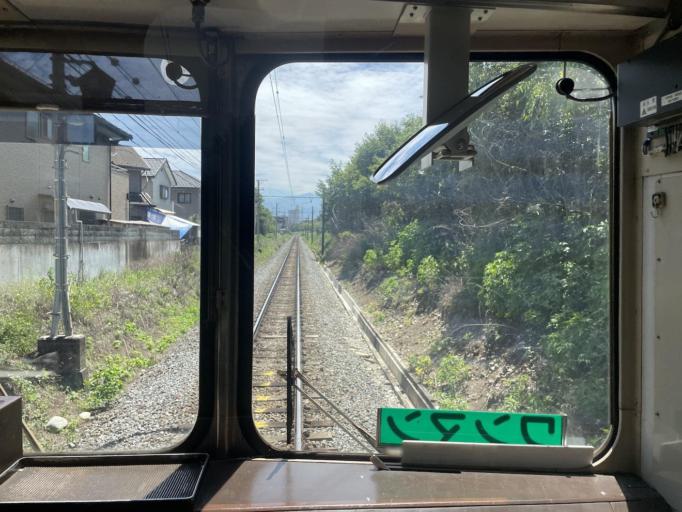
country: JP
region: Saitama
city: Chichibu
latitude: 36.0367
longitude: 139.0986
